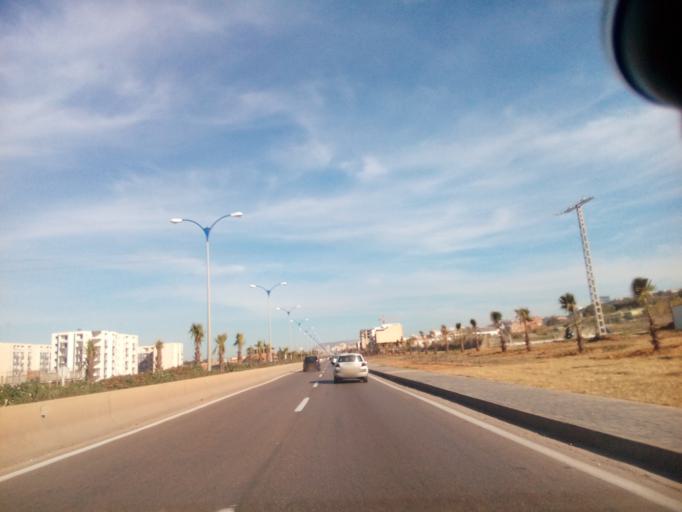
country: DZ
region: Mostaganem
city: Mostaganem
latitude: 35.9051
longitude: 0.0668
